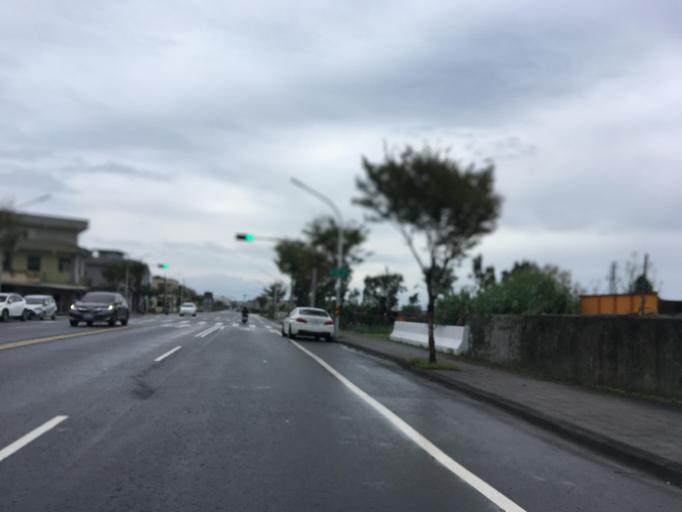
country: TW
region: Taiwan
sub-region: Yilan
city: Yilan
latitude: 24.6357
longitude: 121.7943
